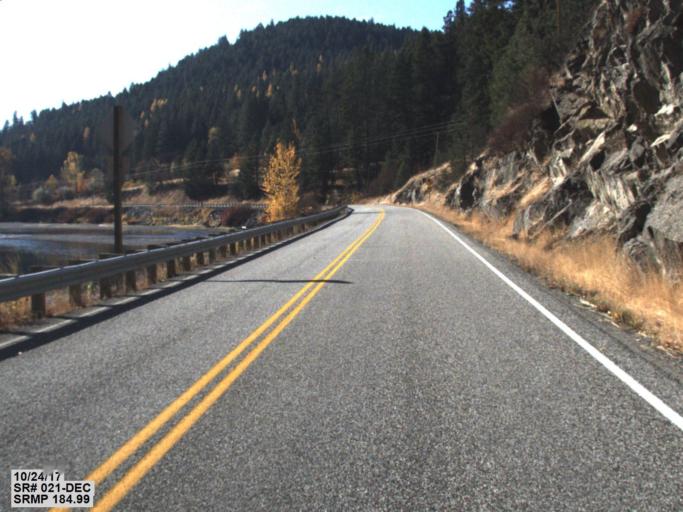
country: CA
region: British Columbia
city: Grand Forks
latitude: 48.9282
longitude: -118.5661
